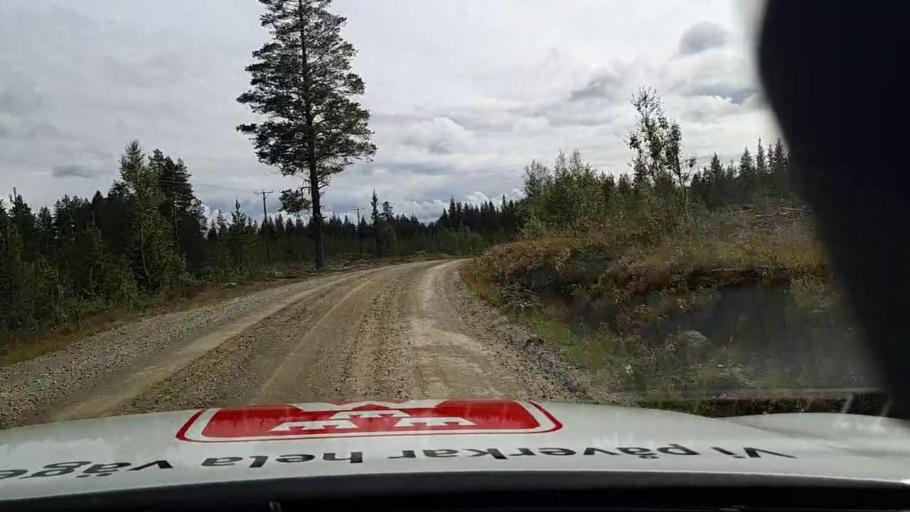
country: SE
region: Jaemtland
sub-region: Are Kommun
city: Jarpen
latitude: 62.5025
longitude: 13.5016
